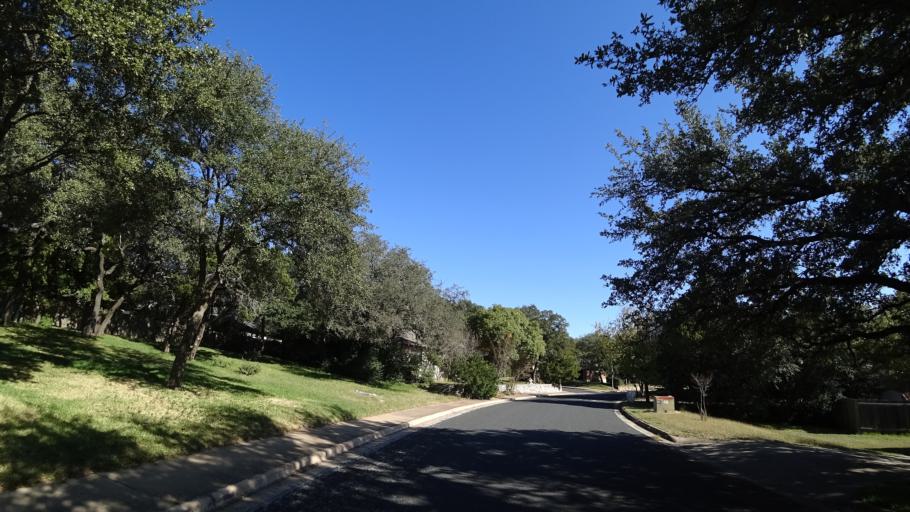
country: US
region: Texas
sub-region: Williamson County
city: Jollyville
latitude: 30.4161
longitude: -97.7713
